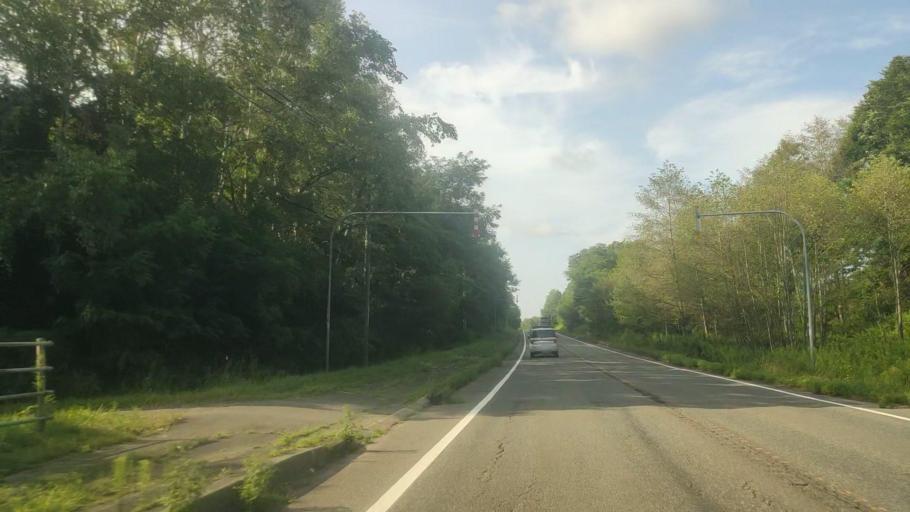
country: JP
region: Hokkaido
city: Chitose
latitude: 42.8685
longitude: 141.8226
